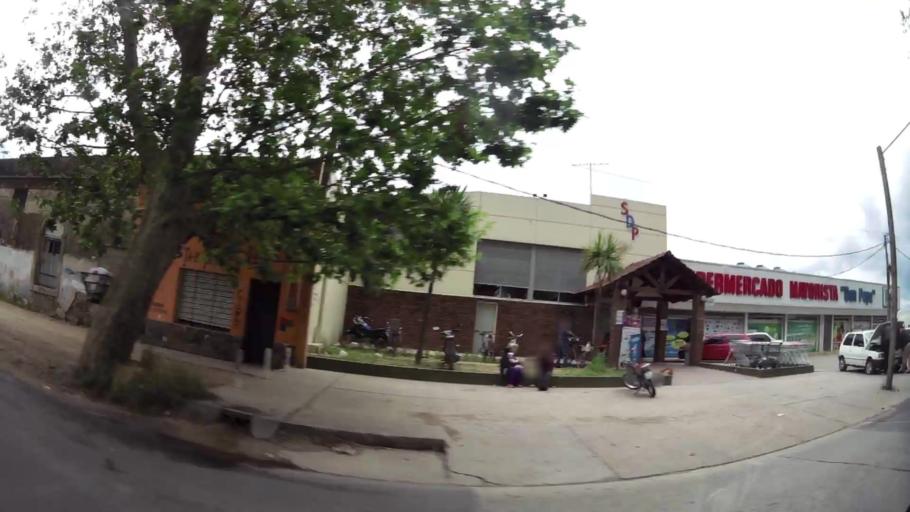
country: UY
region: Canelones
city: Toledo
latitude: -34.8032
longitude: -56.1367
